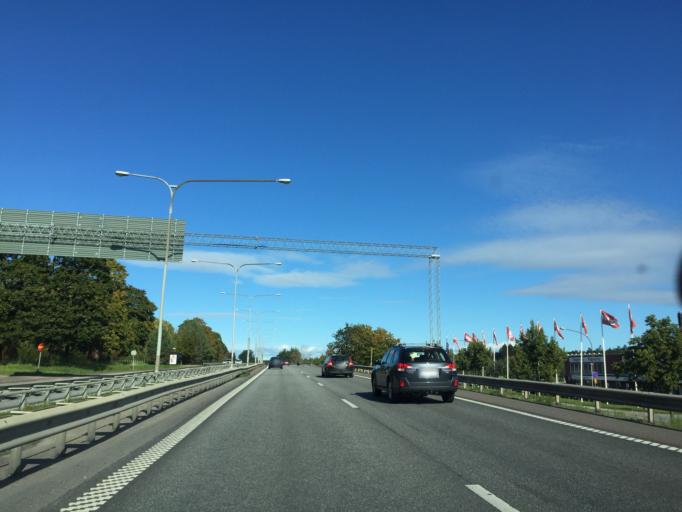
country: SE
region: OErebro
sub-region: Orebro Kommun
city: Orebro
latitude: 59.2985
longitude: 15.2293
